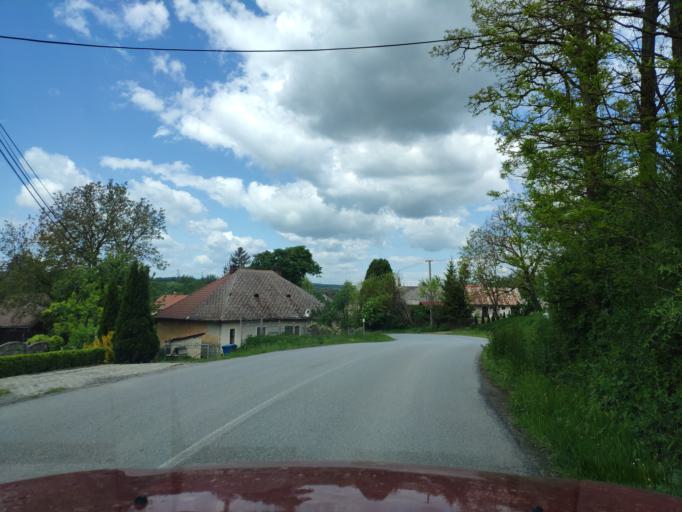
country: SK
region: Kosicky
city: Kosice
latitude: 48.8483
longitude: 21.3199
